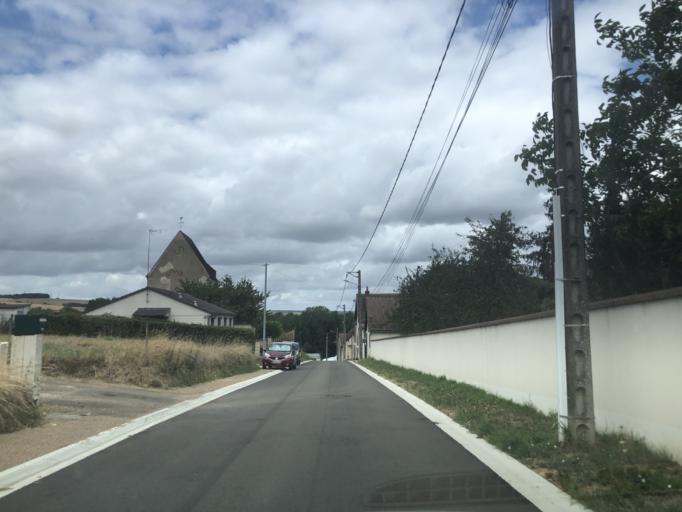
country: FR
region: Bourgogne
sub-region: Departement de l'Yonne
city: Joigny
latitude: 47.9529
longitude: 3.3703
